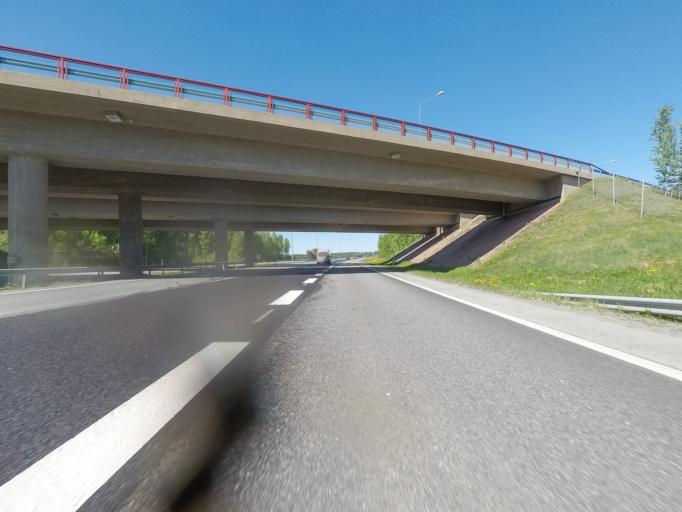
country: FI
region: Pirkanmaa
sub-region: Etelae-Pirkanmaa
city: Toijala
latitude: 61.2038
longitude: 23.8414
